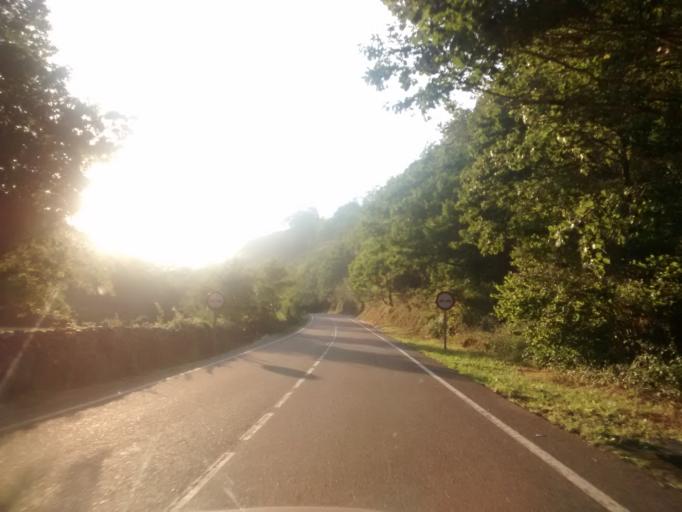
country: ES
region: Cantabria
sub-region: Provincia de Cantabria
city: Ruente
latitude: 43.1524
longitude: -4.2233
